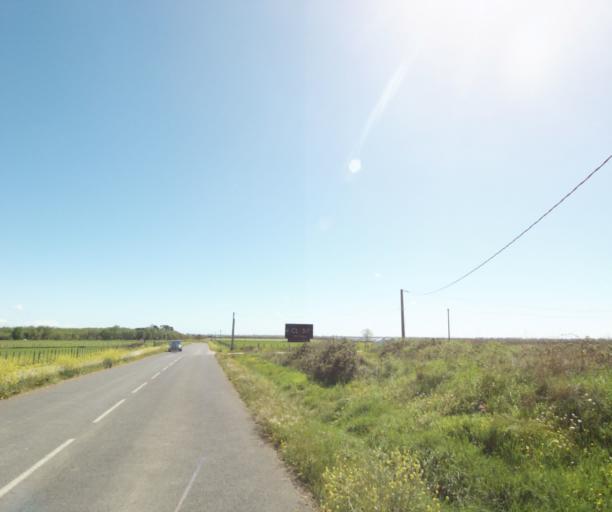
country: FR
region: Languedoc-Roussillon
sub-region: Departement de l'Herault
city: Perols
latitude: 43.5591
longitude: 3.9286
